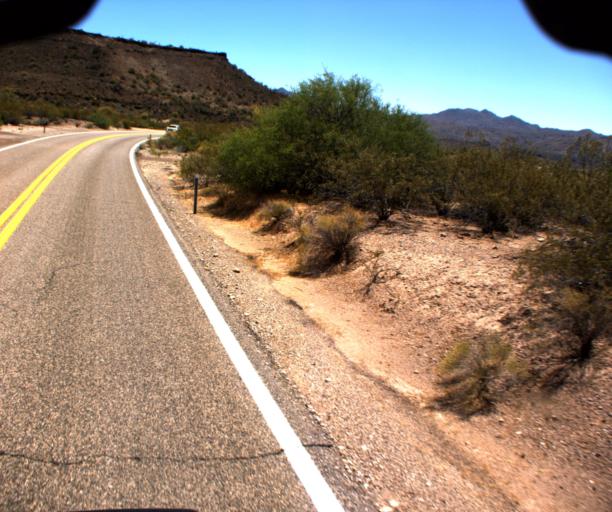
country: US
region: Arizona
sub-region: Yavapai County
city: Bagdad
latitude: 34.4952
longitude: -113.0653
